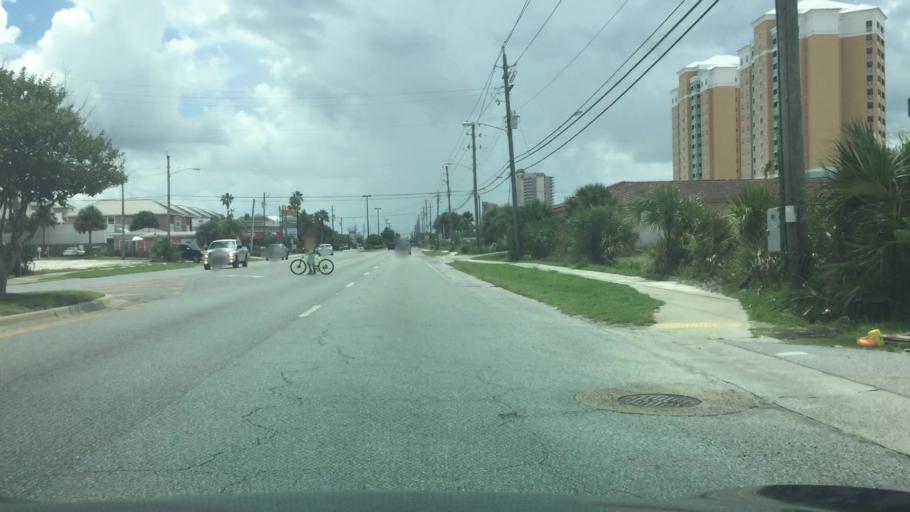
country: US
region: Florida
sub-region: Bay County
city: Panama City Beach
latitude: 30.1619
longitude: -85.7806
